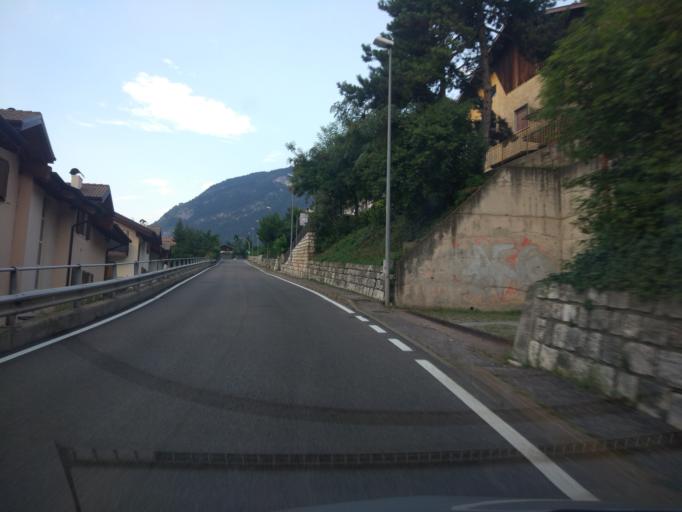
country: IT
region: Trentino-Alto Adige
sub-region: Provincia di Trento
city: Trento
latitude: 46.0839
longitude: 11.1282
